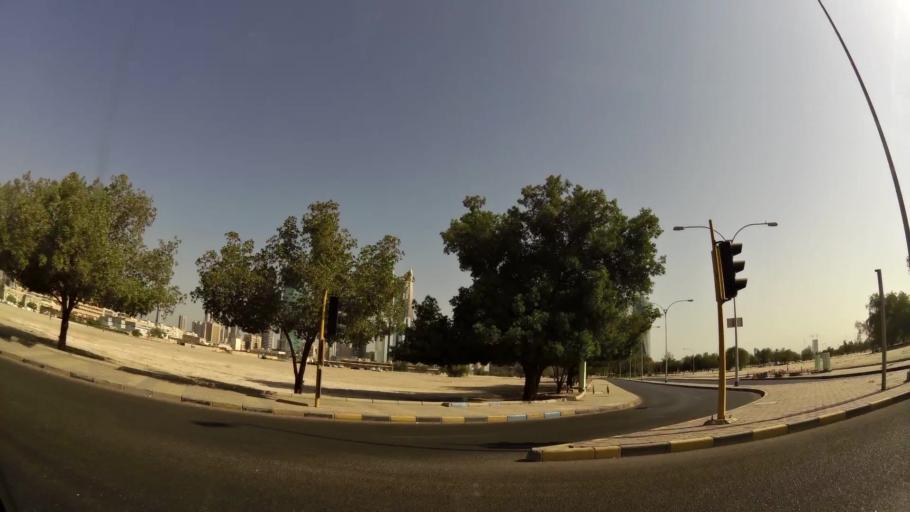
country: KW
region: Al Asimah
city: Kuwait City
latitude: 29.3664
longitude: 47.9829
